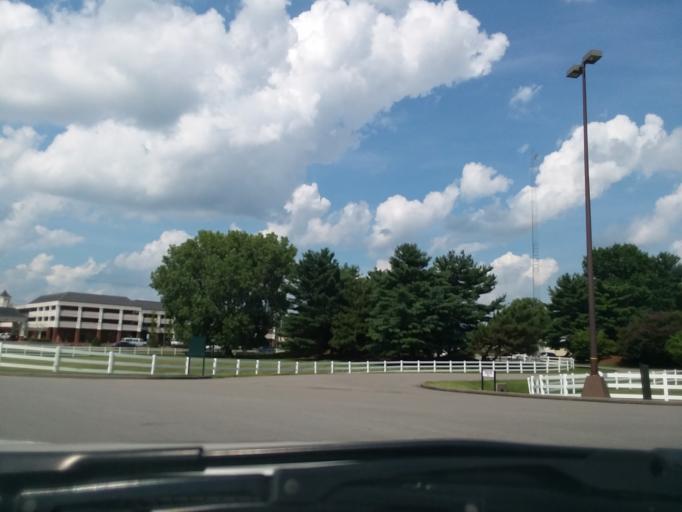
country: US
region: Tennessee
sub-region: Davidson County
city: Lakewood
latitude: 36.2160
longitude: -86.6962
